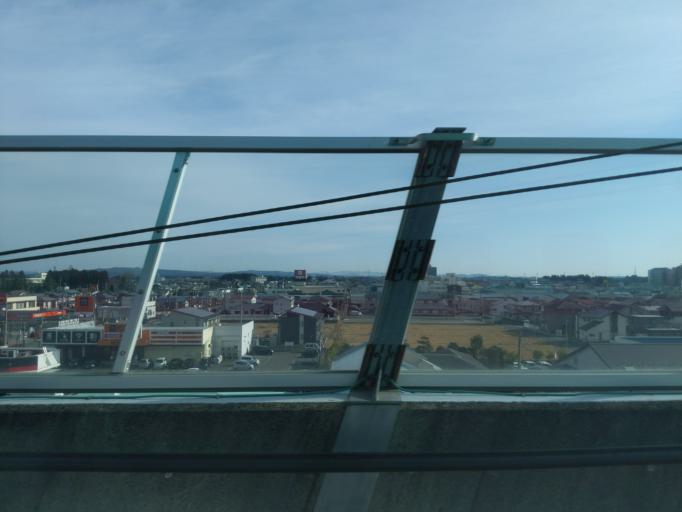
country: JP
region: Miyagi
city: Furukawa
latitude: 38.5750
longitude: 140.9690
